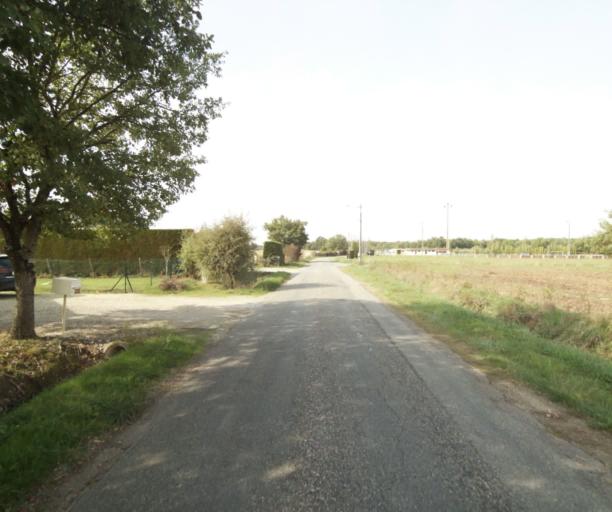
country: FR
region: Midi-Pyrenees
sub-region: Departement du Tarn-et-Garonne
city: Orgueil
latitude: 43.9025
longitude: 1.3995
